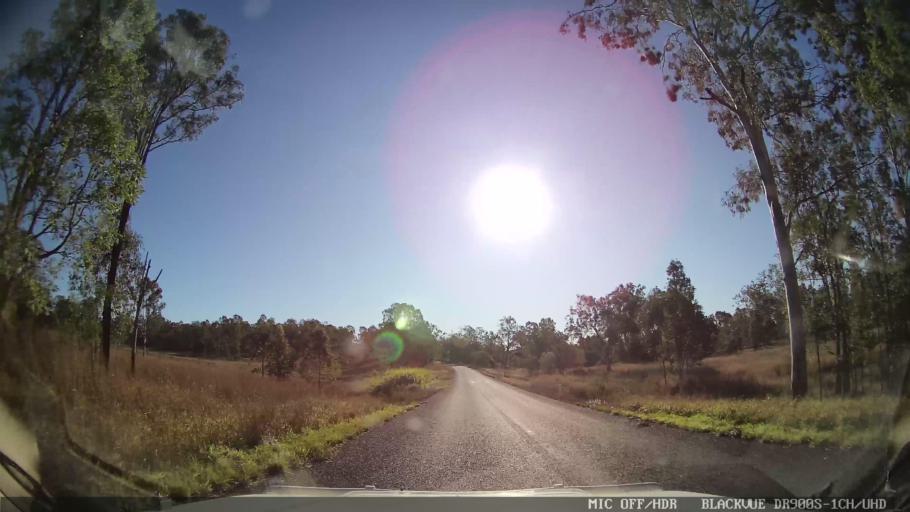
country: AU
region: Queensland
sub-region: Bundaberg
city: Sharon
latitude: -24.8050
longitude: 151.6535
